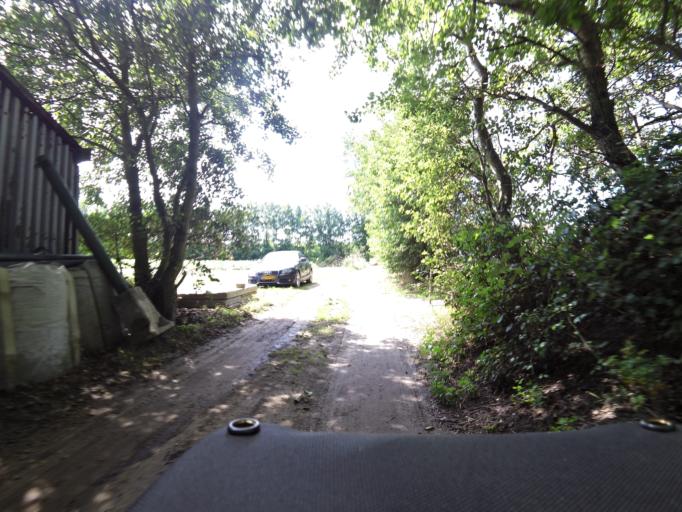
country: NL
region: South Holland
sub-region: Gemeente Goeree-Overflakkee
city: Ouddorp
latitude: 51.8120
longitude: 3.9255
